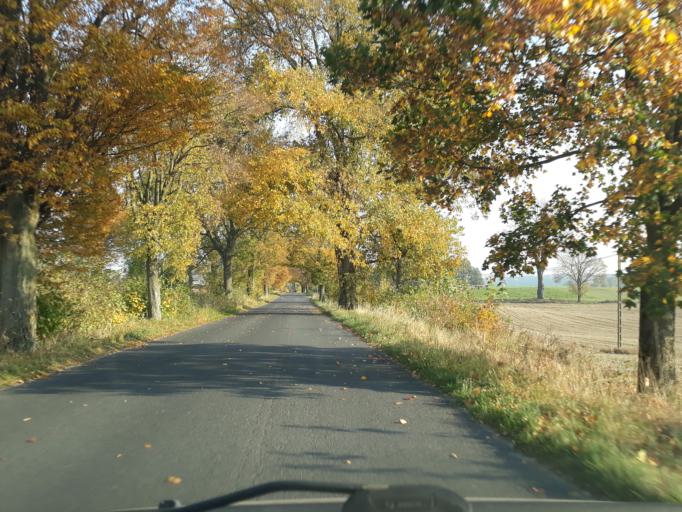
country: PL
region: Kujawsko-Pomorskie
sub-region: Powiat sepolenski
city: Sepolno Krajenskie
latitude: 53.4730
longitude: 17.4741
